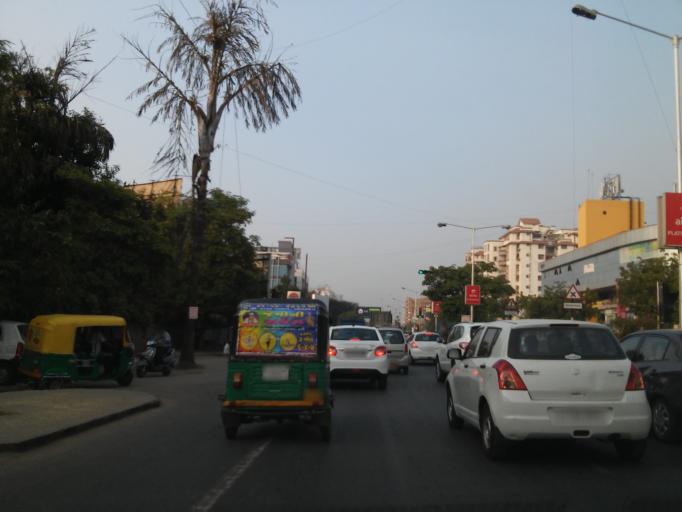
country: IN
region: Gujarat
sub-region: Ahmadabad
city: Sarkhej
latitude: 23.0186
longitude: 72.5300
